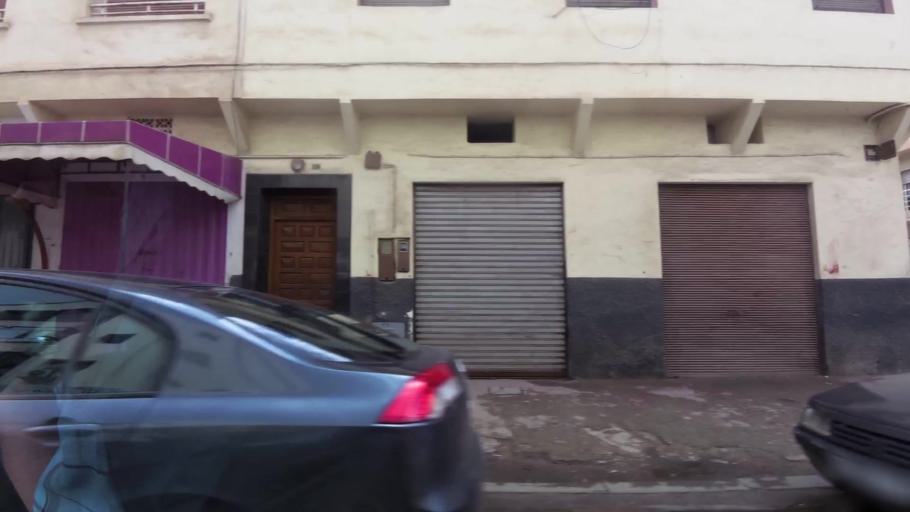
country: MA
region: Chaouia-Ouardigha
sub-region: Settat Province
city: Berrechid
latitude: 33.2676
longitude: -7.5872
